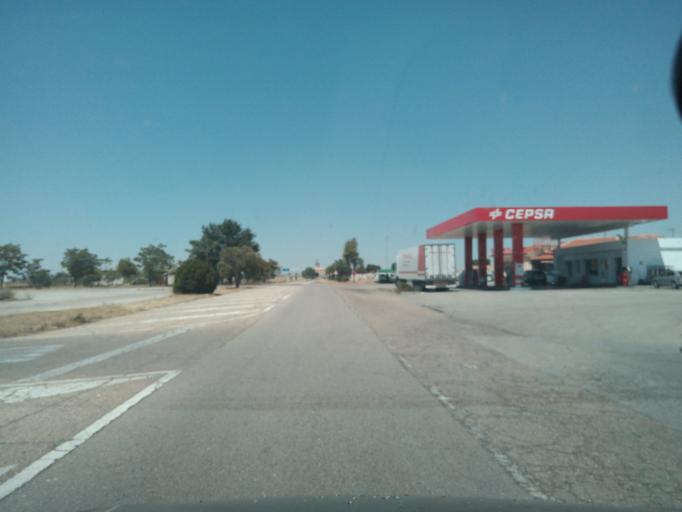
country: ES
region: Castille-La Mancha
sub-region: Province of Toledo
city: Tembleque
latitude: 39.7782
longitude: -3.4784
